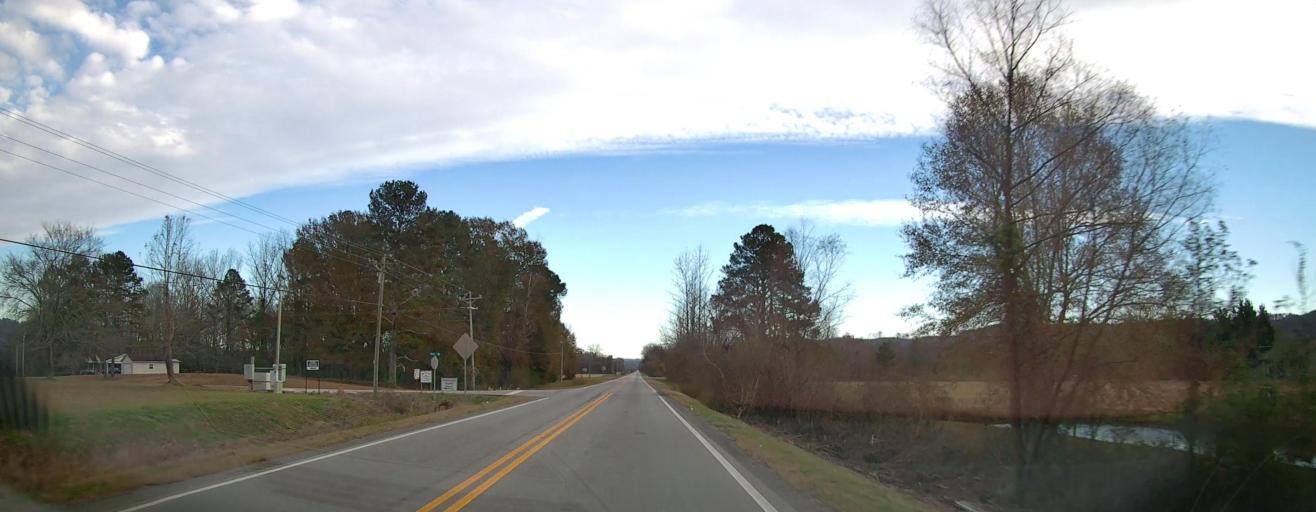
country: US
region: Alabama
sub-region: Morgan County
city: Falkville
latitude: 34.4115
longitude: -86.6979
